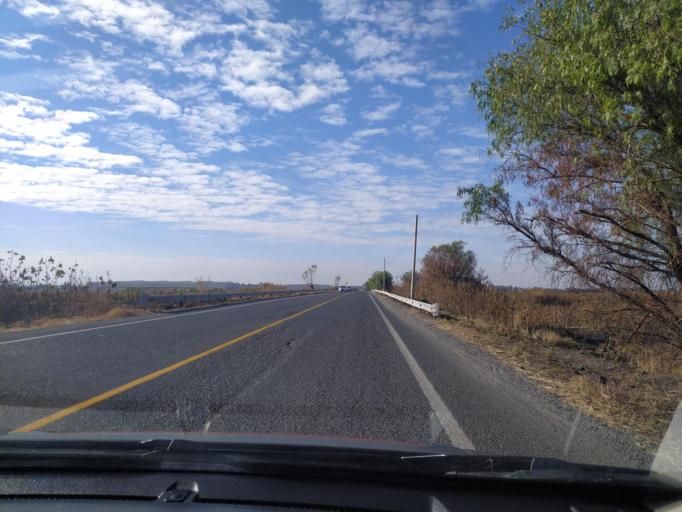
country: MX
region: Guanajuato
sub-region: San Francisco del Rincon
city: Fraccionamiento la Mezquitera
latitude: 21.0102
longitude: -101.8292
